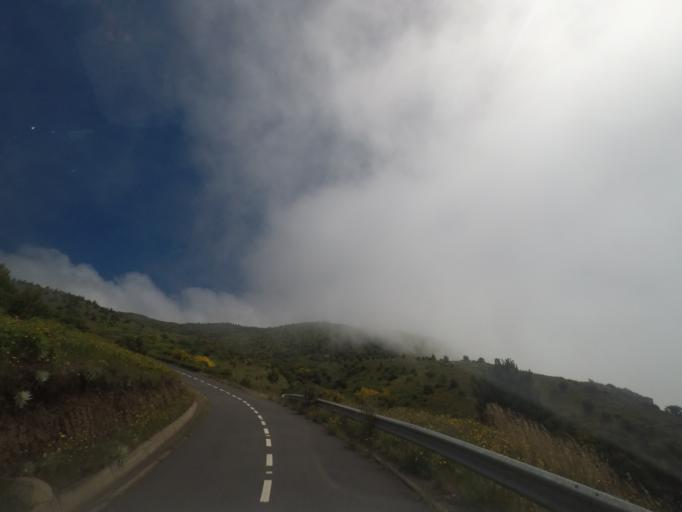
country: PT
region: Madeira
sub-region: Camara de Lobos
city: Curral das Freiras
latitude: 32.7060
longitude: -16.9392
